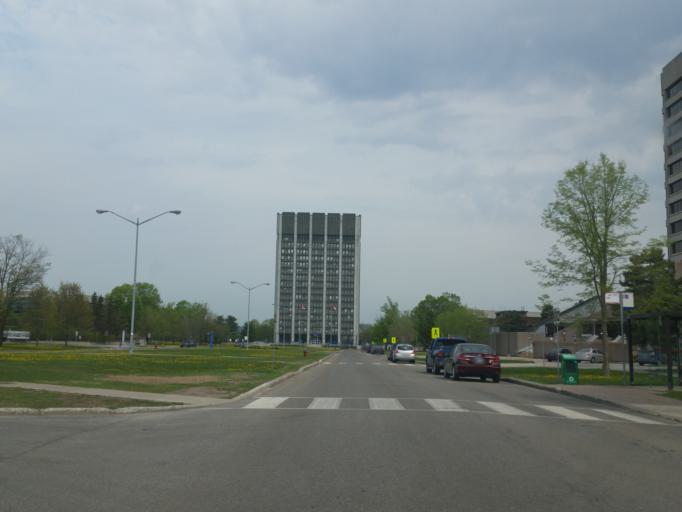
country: CA
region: Ontario
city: Ottawa
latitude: 45.4056
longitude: -75.7352
